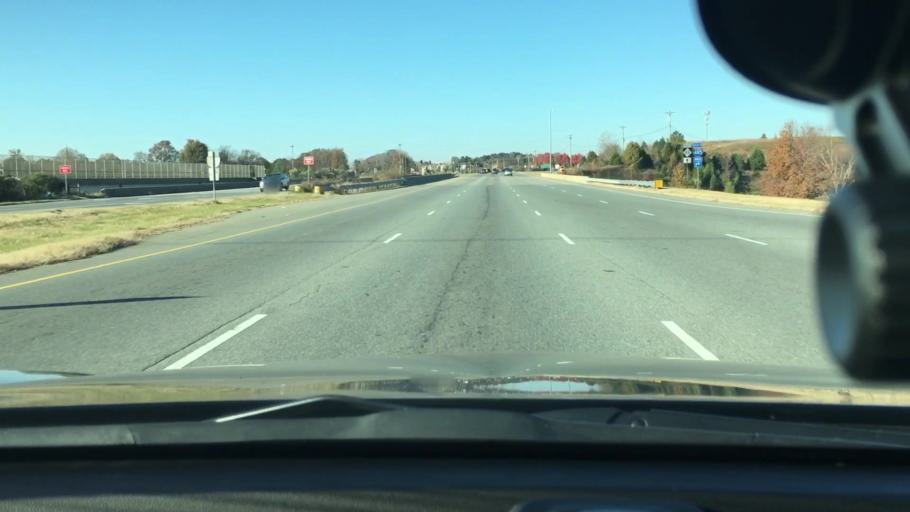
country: US
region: North Carolina
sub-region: Cabarrus County
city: Harrisburg
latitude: 35.3127
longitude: -80.7064
